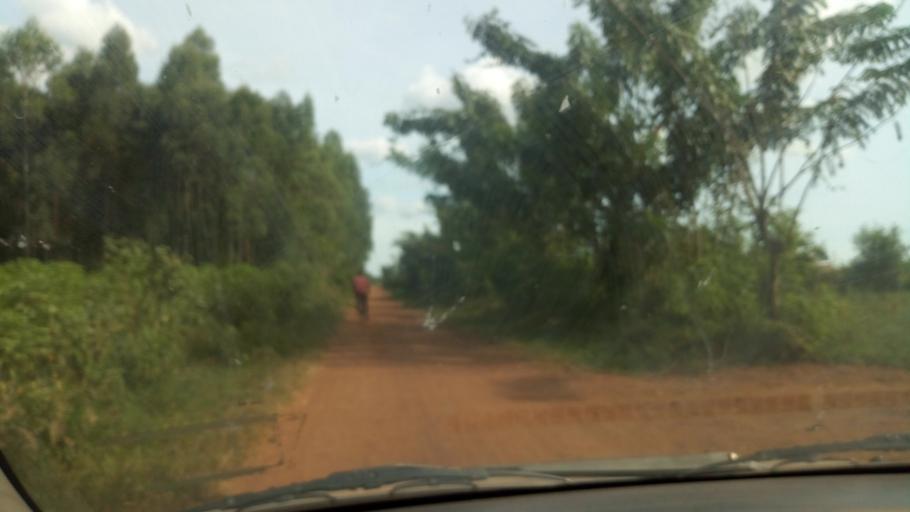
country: UG
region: Western Region
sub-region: Kiryandongo District
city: Kiryandongo
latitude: 1.8143
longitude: 31.9376
